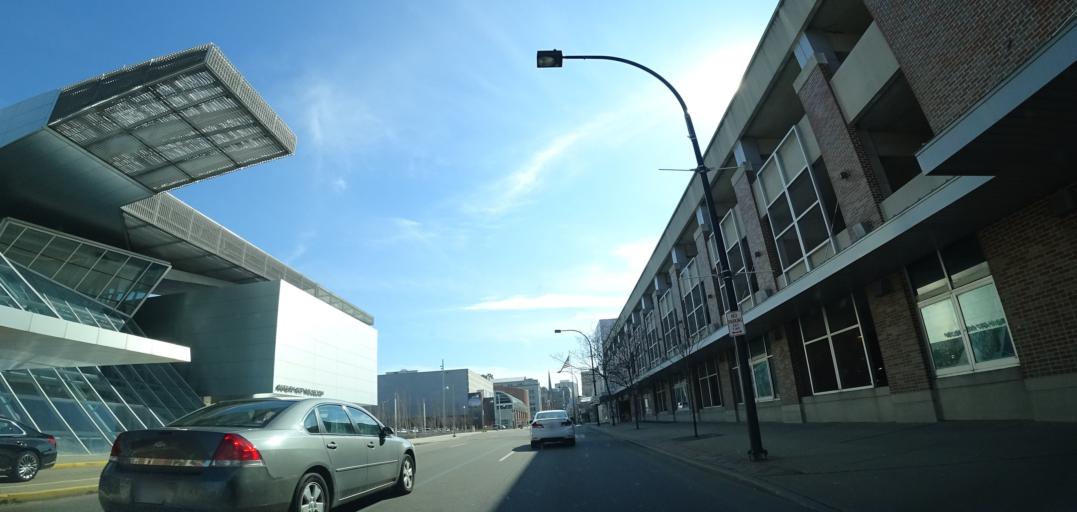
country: US
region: Ohio
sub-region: Summit County
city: Akron
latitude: 41.0848
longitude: -81.5157
